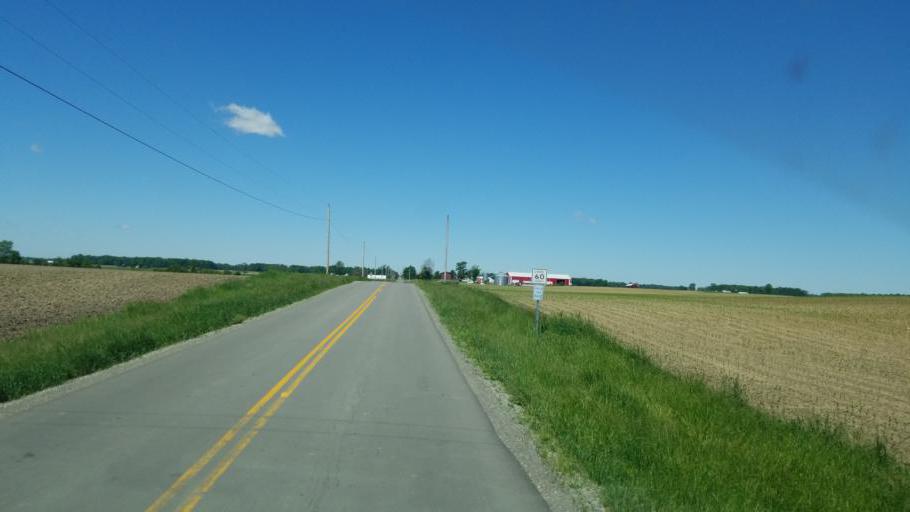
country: US
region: Ohio
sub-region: Shelby County
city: Jackson Center
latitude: 40.4174
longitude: -83.9746
